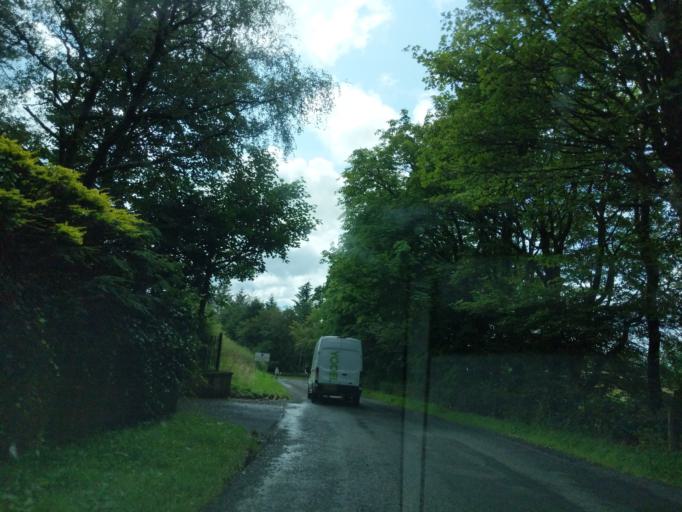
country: GB
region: Scotland
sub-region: East Ayrshire
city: Stewarton
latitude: 55.7142
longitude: -4.5250
